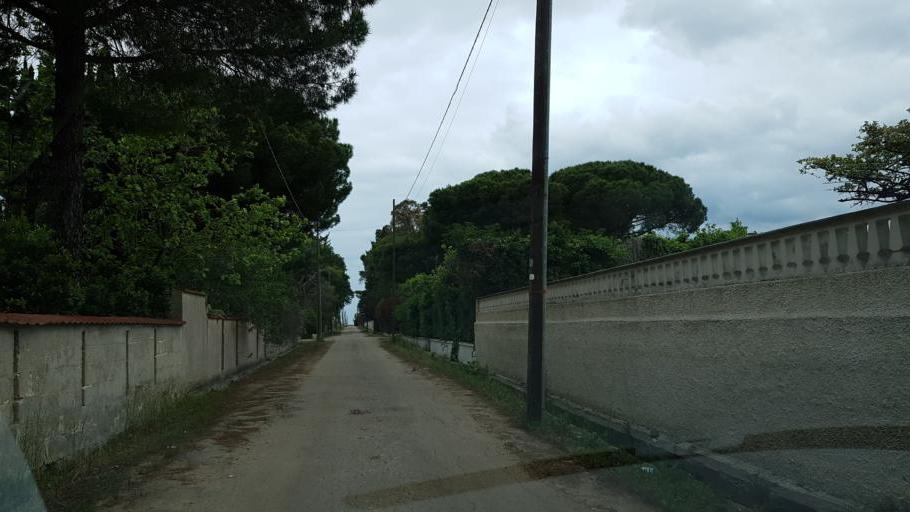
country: IT
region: Apulia
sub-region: Provincia di Brindisi
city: Brindisi
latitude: 40.6348
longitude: 17.8971
